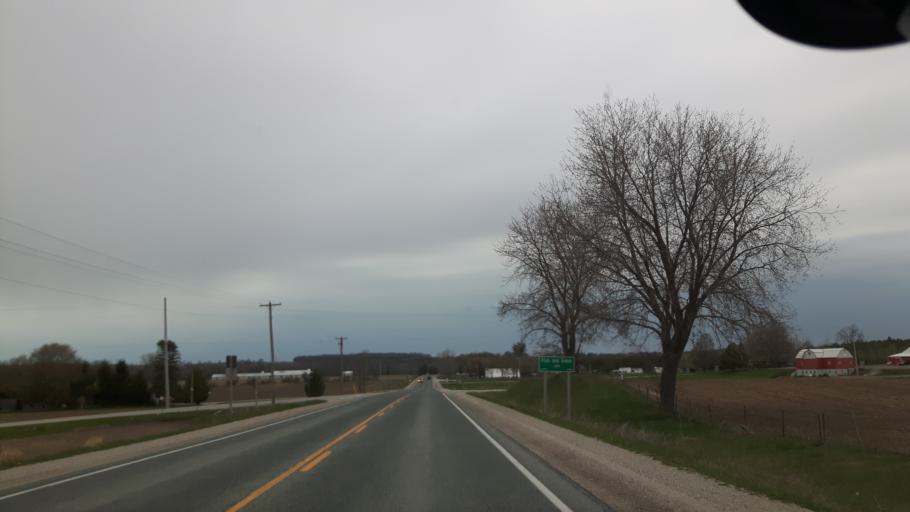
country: CA
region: Ontario
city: Bluewater
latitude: 43.6348
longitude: -81.5804
